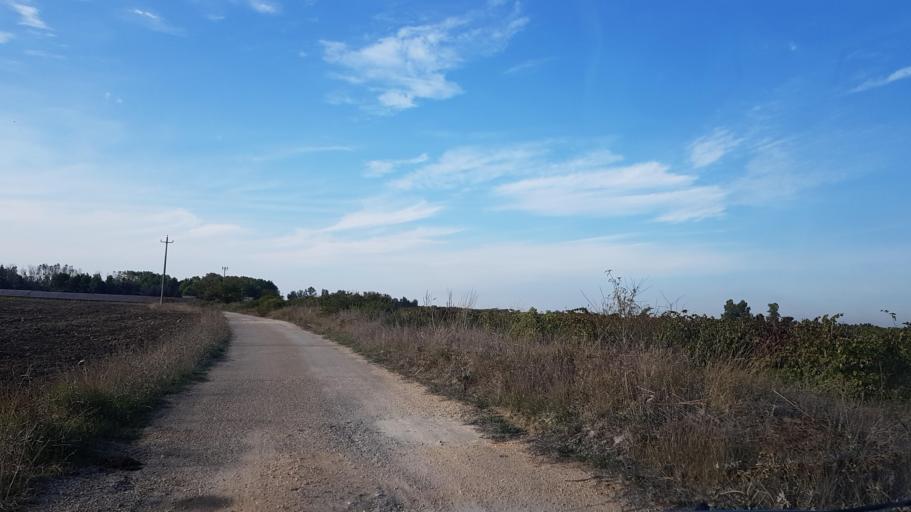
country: IT
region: Apulia
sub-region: Provincia di Brindisi
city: San Pancrazio Salentino
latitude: 40.4878
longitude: 17.8577
